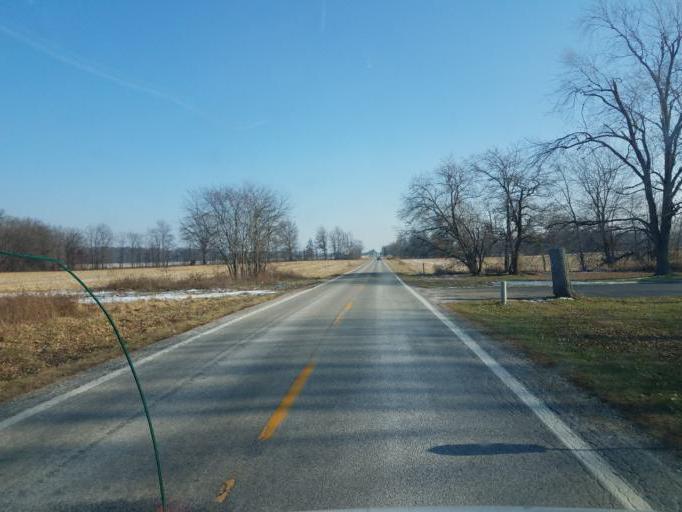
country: US
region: Ohio
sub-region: Morrow County
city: Cardington
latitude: 40.5325
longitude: -82.9844
